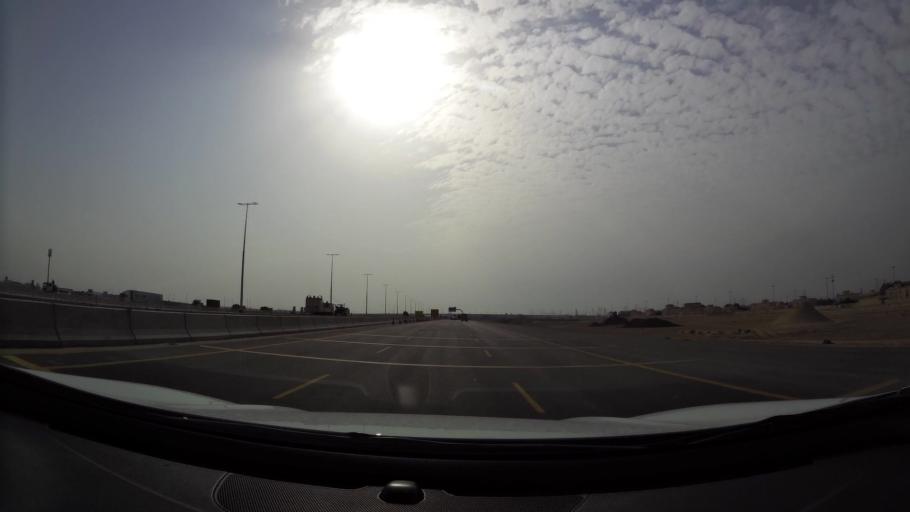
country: AE
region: Abu Dhabi
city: Abu Dhabi
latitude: 24.2933
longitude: 54.5675
